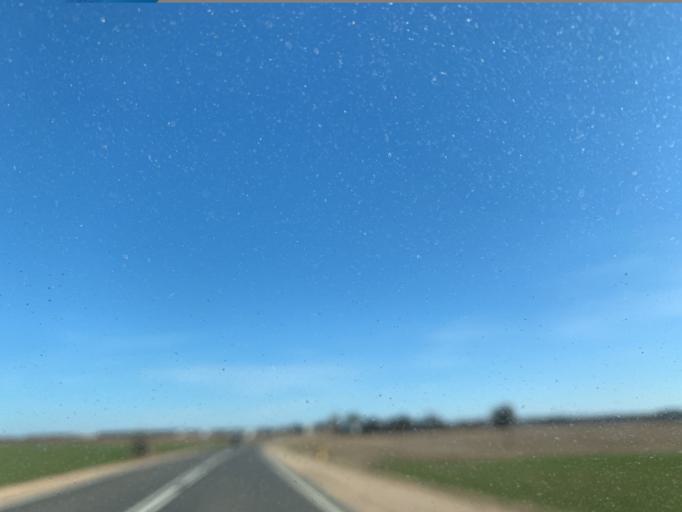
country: BY
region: Minsk
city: Nyasvizh
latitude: 53.2250
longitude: 26.7108
